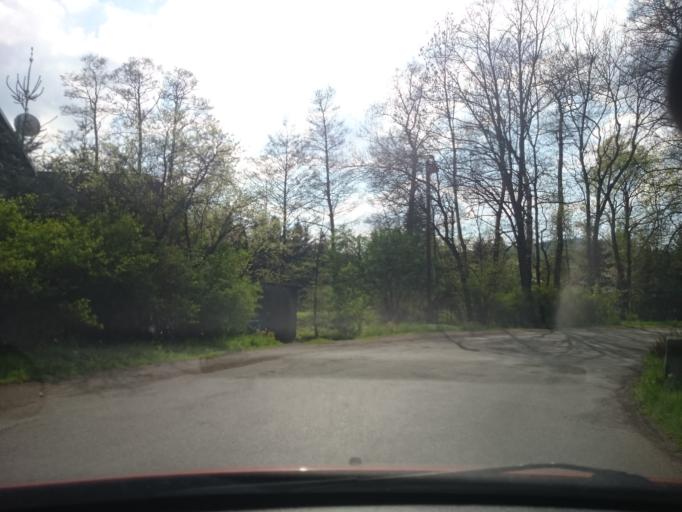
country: PL
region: Lower Silesian Voivodeship
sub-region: Powiat klodzki
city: Bystrzyca Klodzka
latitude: 50.3018
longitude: 16.6288
